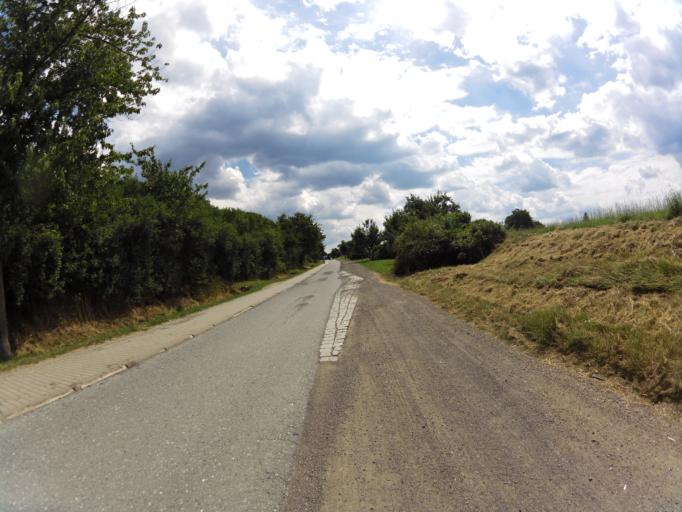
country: DE
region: Thuringia
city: Burgk
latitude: 50.5070
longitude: 11.7265
